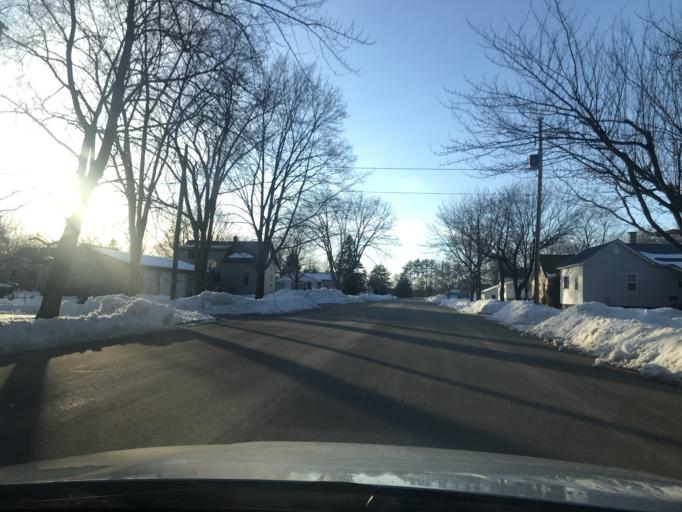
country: US
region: Wisconsin
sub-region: Marinette County
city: Peshtigo
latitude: 45.0578
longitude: -87.7407
